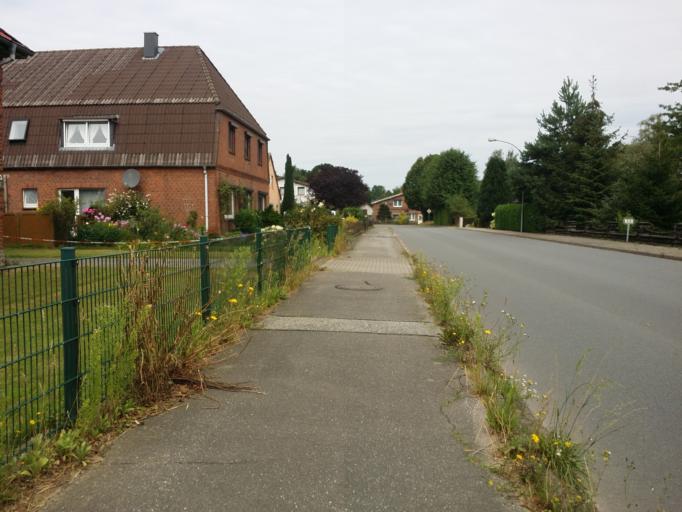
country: DE
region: Schleswig-Holstein
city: Huje
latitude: 53.9753
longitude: 9.4371
